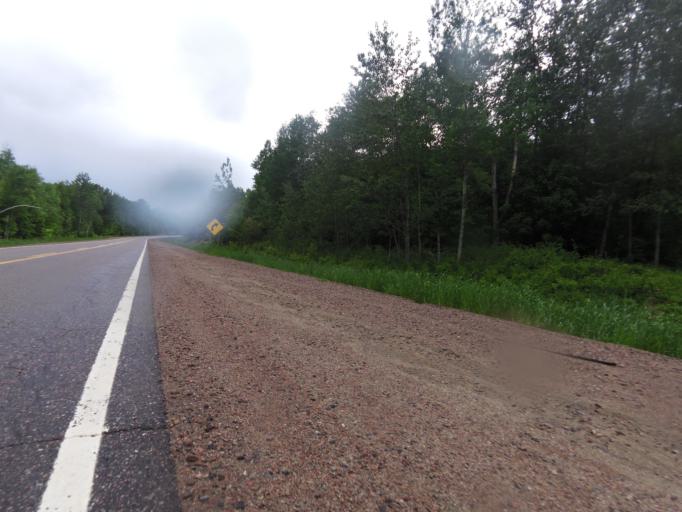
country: CA
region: Quebec
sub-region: Outaouais
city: Shawville
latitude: 45.9074
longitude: -76.2664
